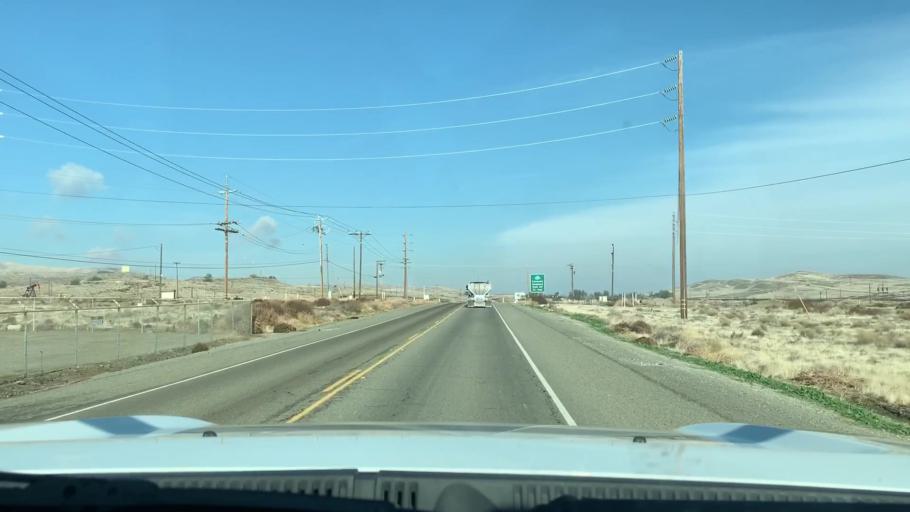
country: US
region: California
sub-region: Fresno County
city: Coalinga
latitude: 36.2374
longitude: -120.3143
